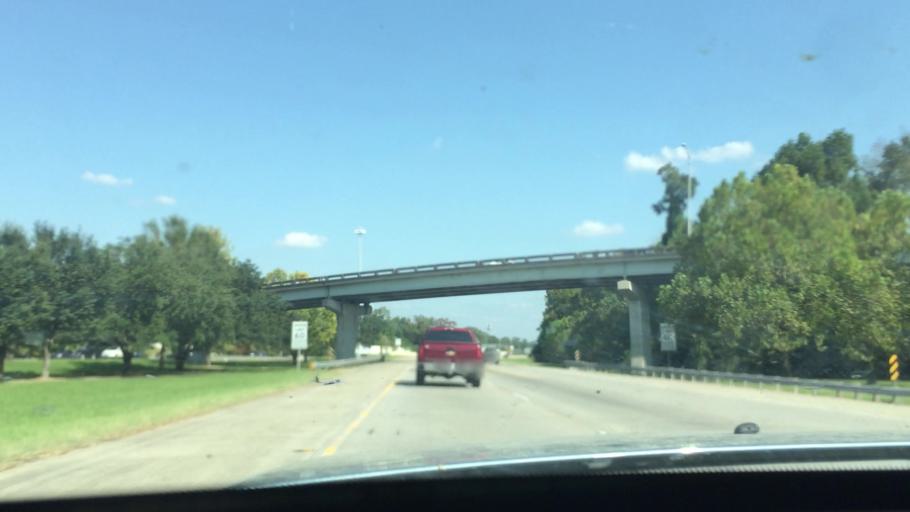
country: US
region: Louisiana
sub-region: East Baton Rouge Parish
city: Westminster
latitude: 30.4184
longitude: -91.1143
